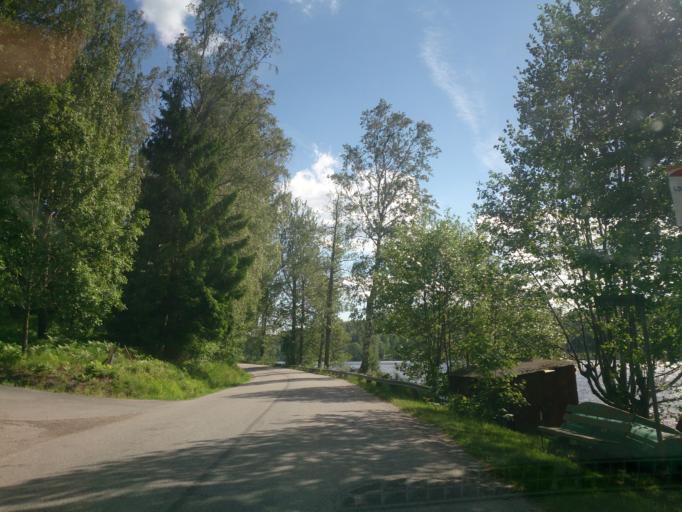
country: SE
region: OEstergoetland
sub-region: Norrkopings Kommun
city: Jursla
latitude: 58.7157
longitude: 16.1547
